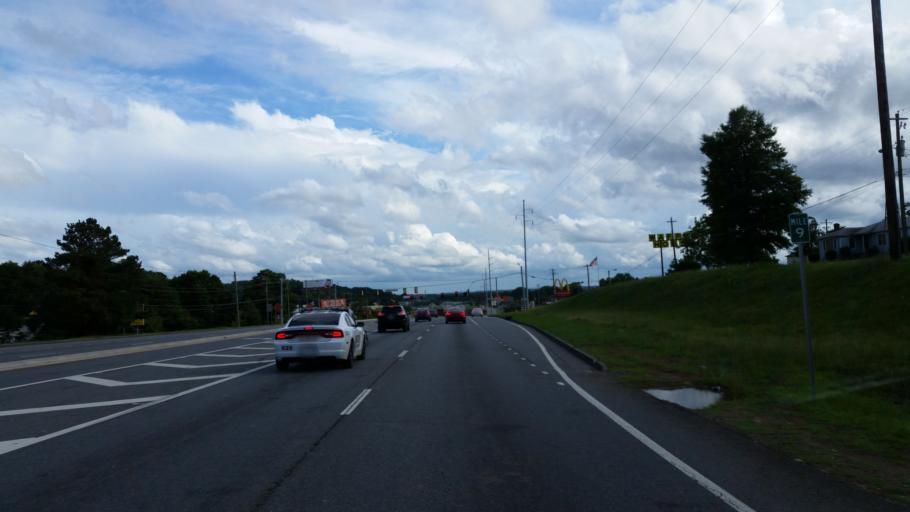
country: US
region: Georgia
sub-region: Bartow County
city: Cartersville
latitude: 34.1783
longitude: -84.7858
